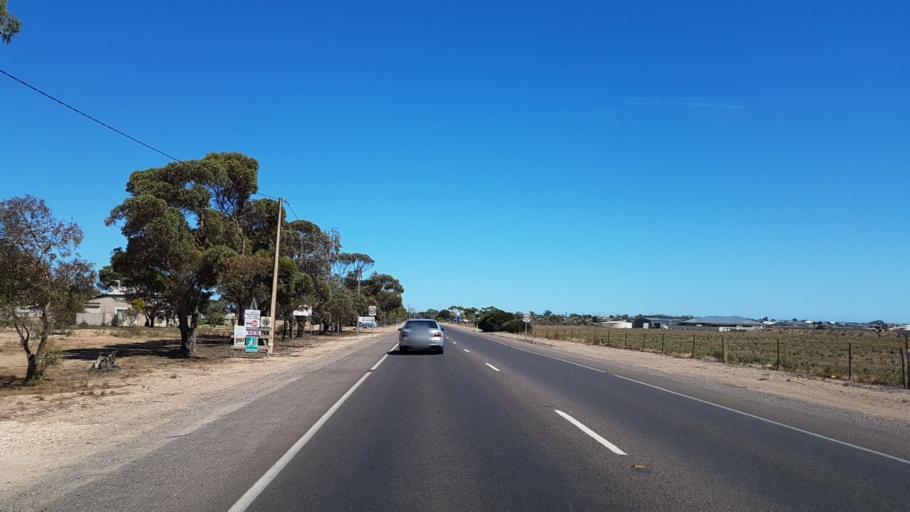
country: AU
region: South Australia
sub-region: Copper Coast
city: Wallaroo
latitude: -33.9393
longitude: 137.6490
